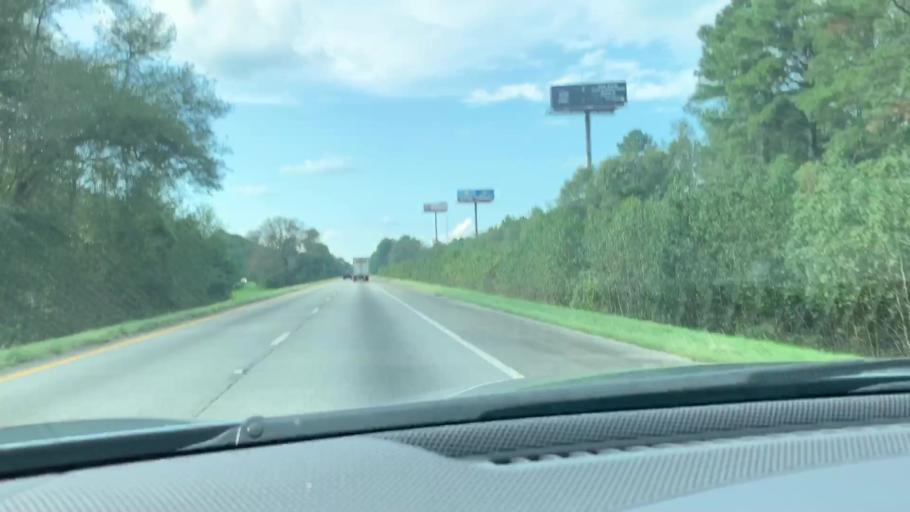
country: US
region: South Carolina
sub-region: Dorchester County
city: Saint George
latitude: 33.3516
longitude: -80.5831
